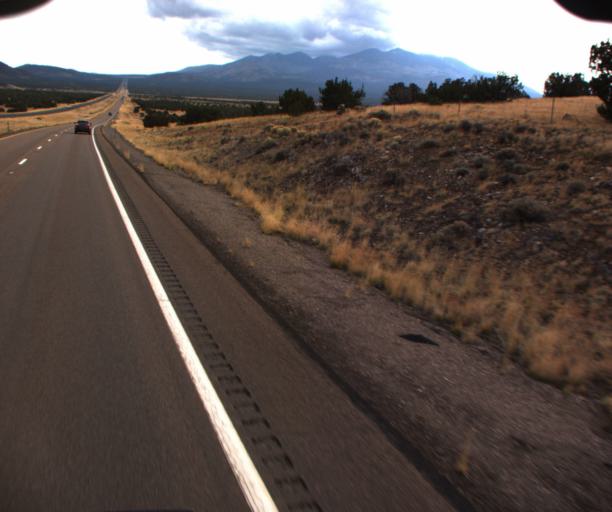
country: US
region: Arizona
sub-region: Coconino County
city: Flagstaff
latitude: 35.4693
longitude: -111.5586
